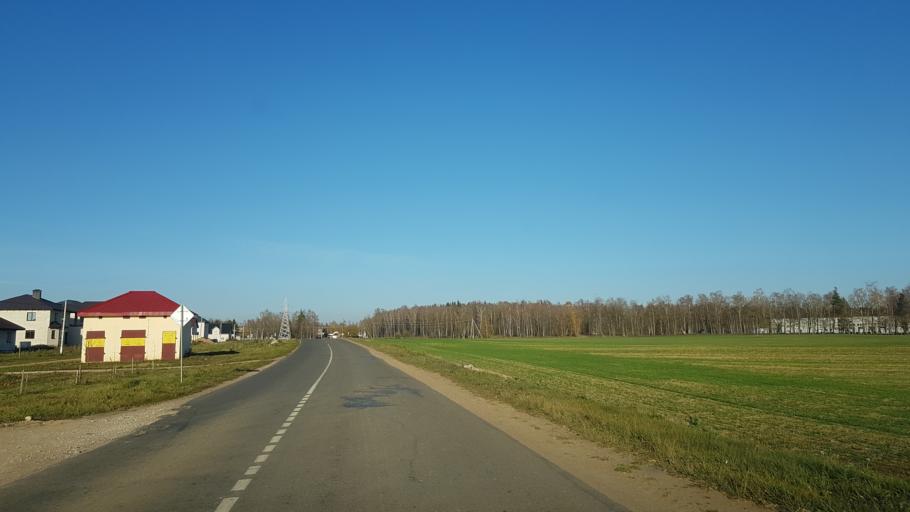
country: BY
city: Fanipol
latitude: 53.7260
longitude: 27.3286
